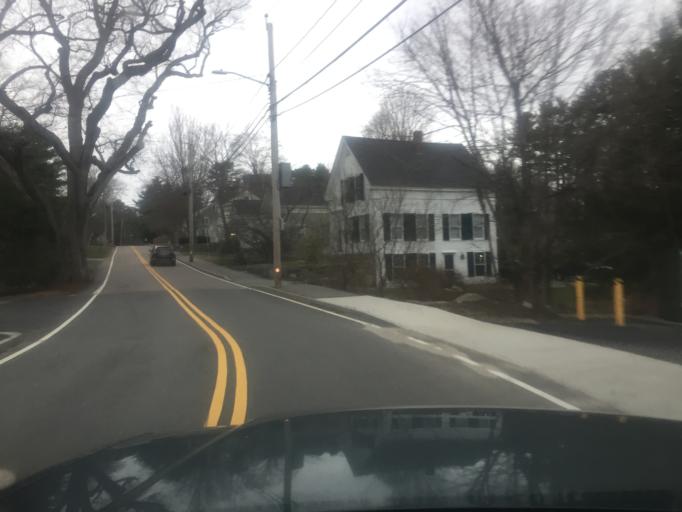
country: US
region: Massachusetts
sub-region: Norfolk County
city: Medway
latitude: 42.1444
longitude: -71.4331
